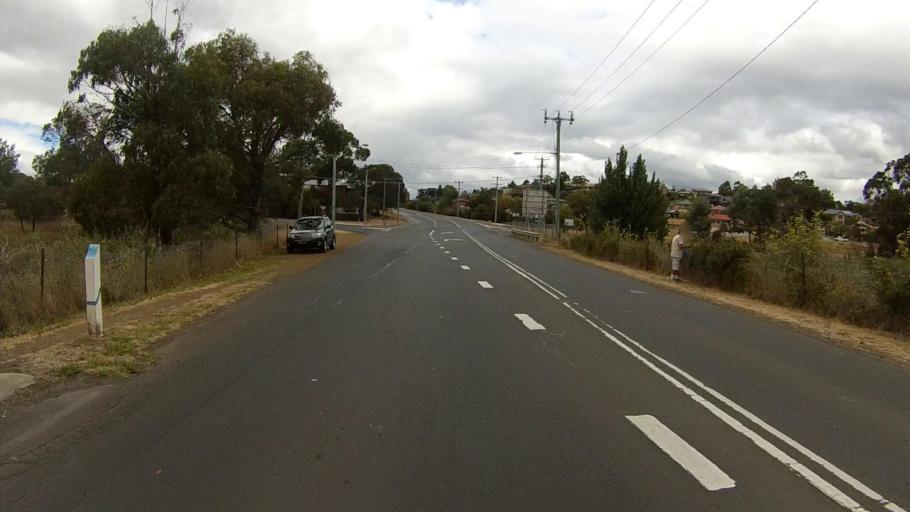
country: AU
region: Tasmania
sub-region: Glenorchy
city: Austins Ferry
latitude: -42.7653
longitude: 147.2429
